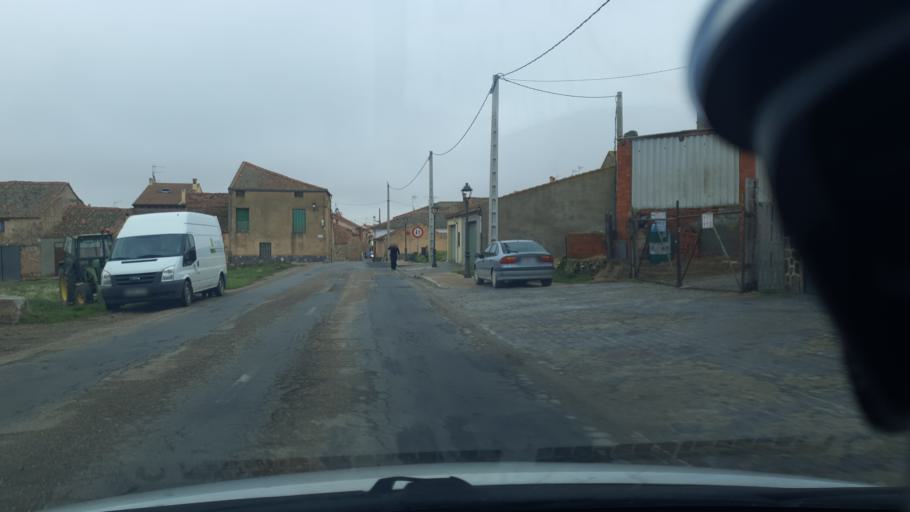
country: ES
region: Castille and Leon
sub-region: Provincia de Segovia
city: Valseca
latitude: 40.9985
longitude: -4.1761
